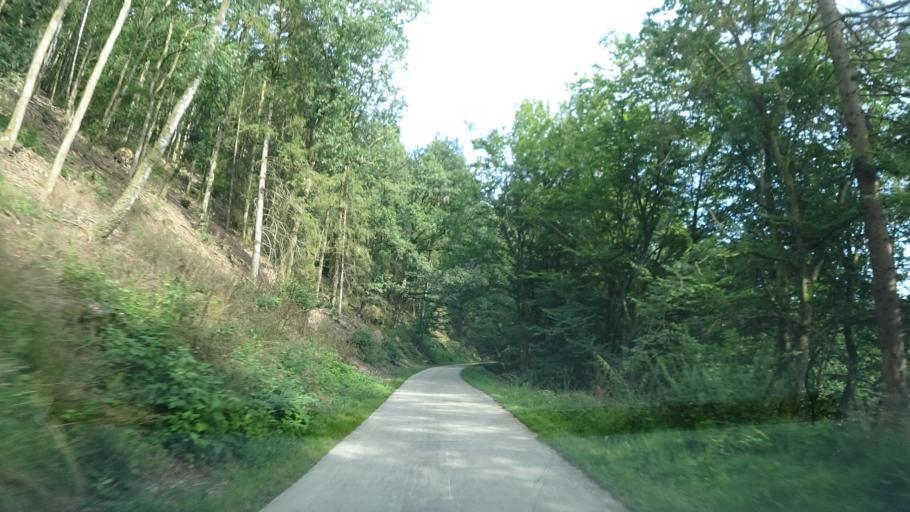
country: BE
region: Wallonia
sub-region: Province du Luxembourg
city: Herbeumont
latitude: 49.7725
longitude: 5.2476
